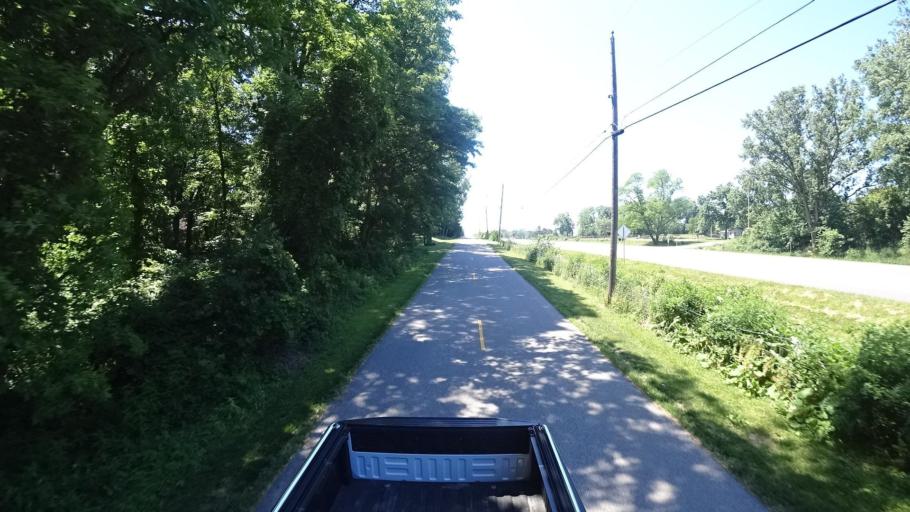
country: US
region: Indiana
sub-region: Porter County
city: Burns Harbor
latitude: 41.6135
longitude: -87.1254
